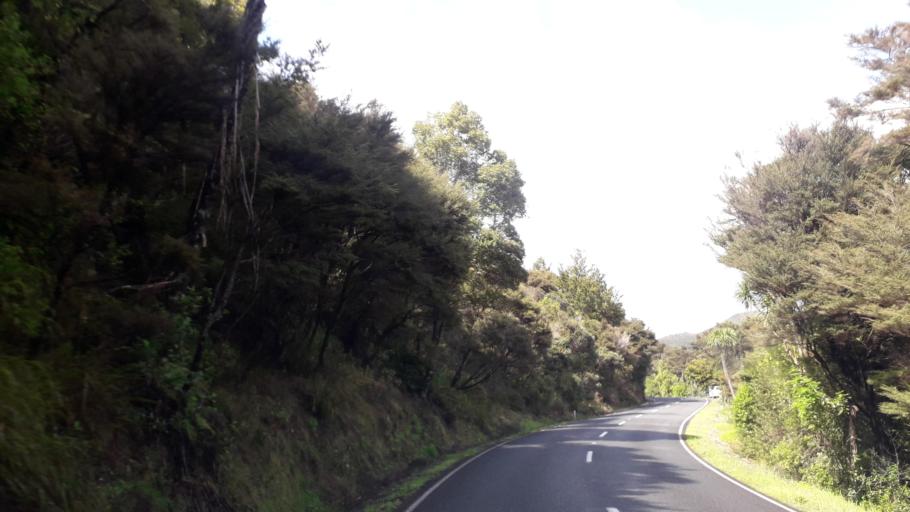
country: NZ
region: Northland
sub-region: Far North District
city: Paihia
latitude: -35.2529
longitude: 174.2631
